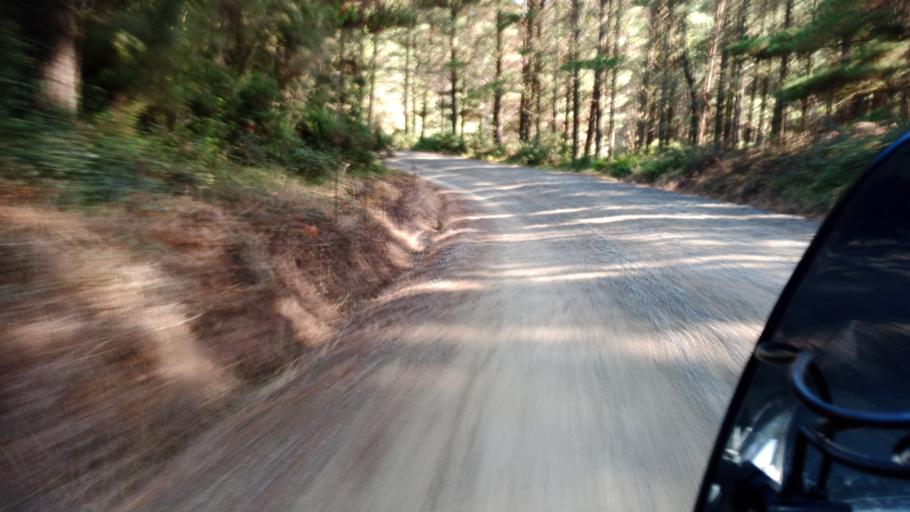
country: NZ
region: Hawke's Bay
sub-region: Wairoa District
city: Wairoa
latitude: -38.9306
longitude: 177.2261
